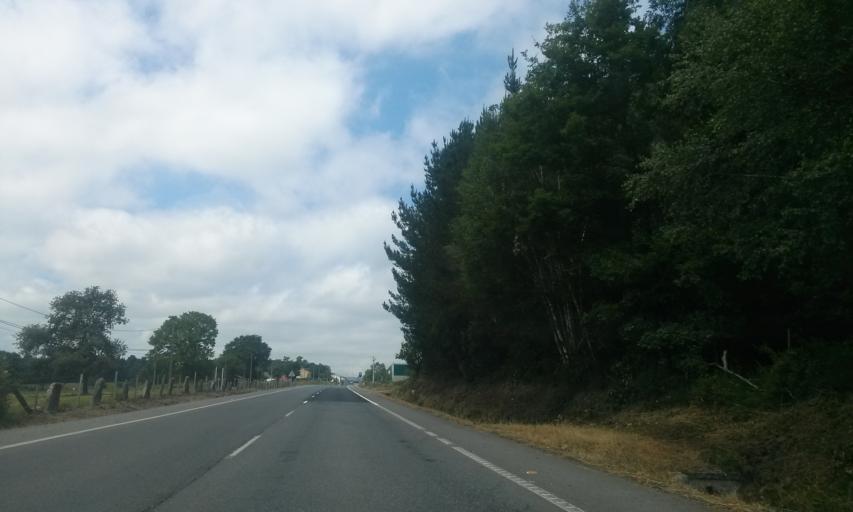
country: ES
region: Galicia
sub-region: Provincia de Lugo
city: Friol
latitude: 43.0317
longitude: -7.7729
